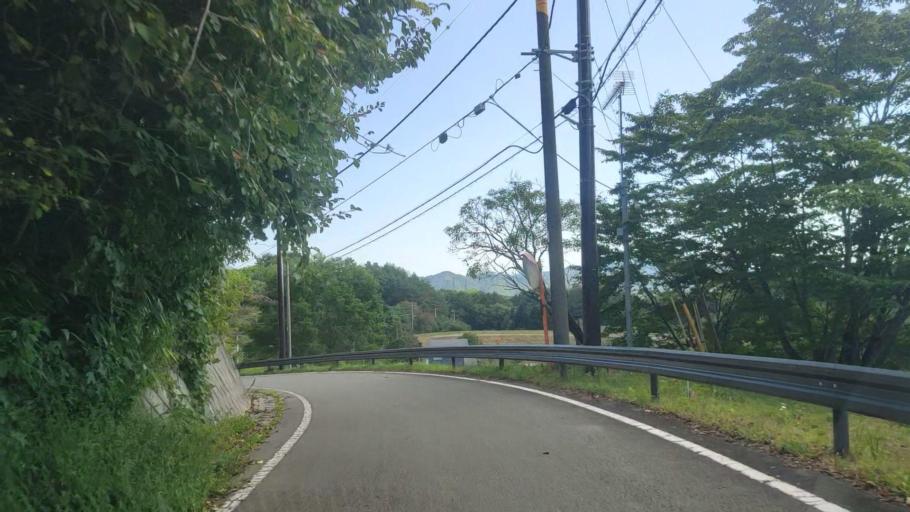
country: JP
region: Gunma
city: Nakanojomachi
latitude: 36.6425
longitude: 138.6193
